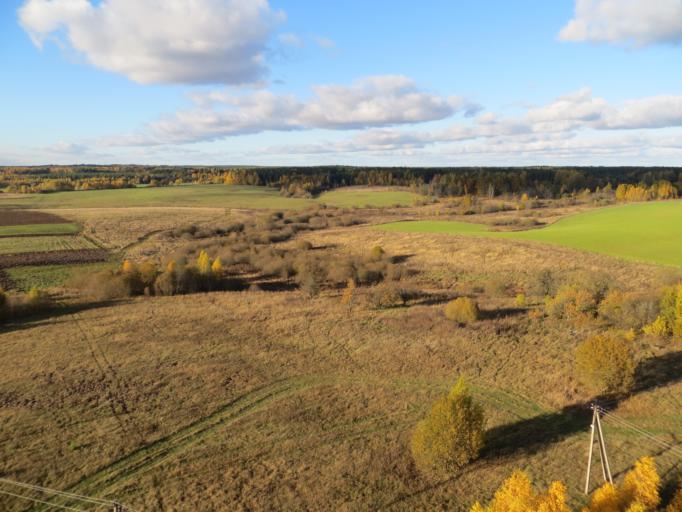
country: LT
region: Vilnius County
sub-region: Vilniaus Rajonas
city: Vievis
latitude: 54.8673
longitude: 24.9127
